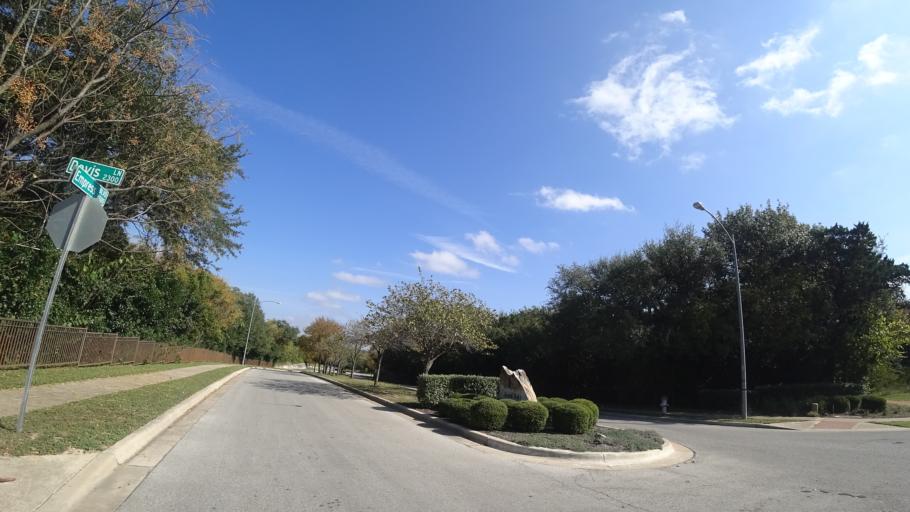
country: US
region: Texas
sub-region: Travis County
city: Shady Hollow
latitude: 30.1875
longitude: -97.8195
